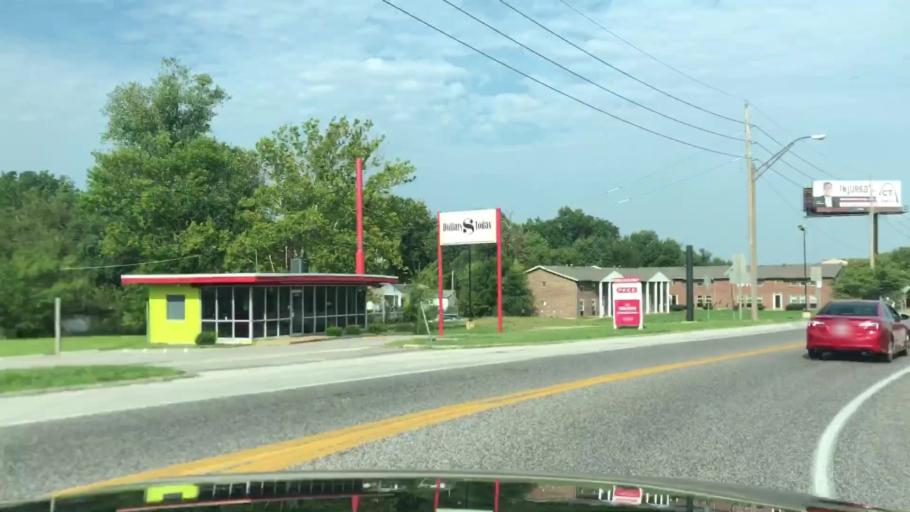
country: US
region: Missouri
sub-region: Saint Louis County
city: Woodson Terrace
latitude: 38.7315
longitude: -90.3489
